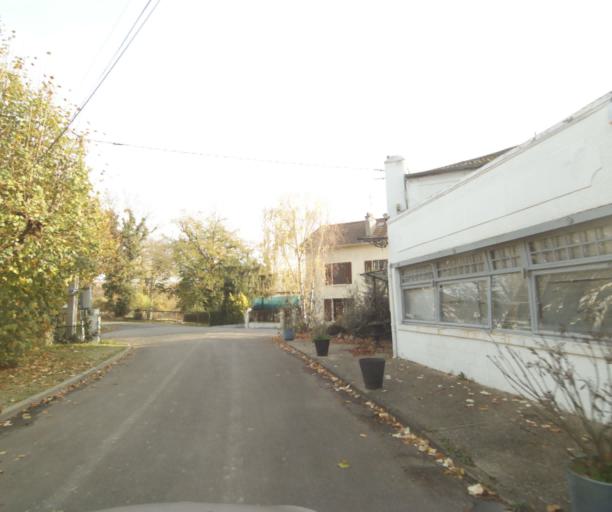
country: FR
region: Ile-de-France
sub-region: Departement des Yvelines
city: Chanteloup-les-Vignes
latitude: 48.9691
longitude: 2.0458
